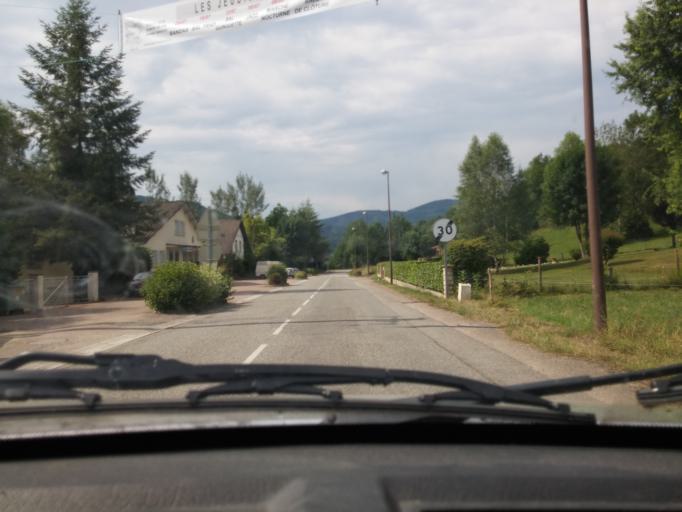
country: FR
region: Midi-Pyrenees
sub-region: Departement de l'Ariege
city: Saint-Girons
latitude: 42.8766
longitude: 1.2171
